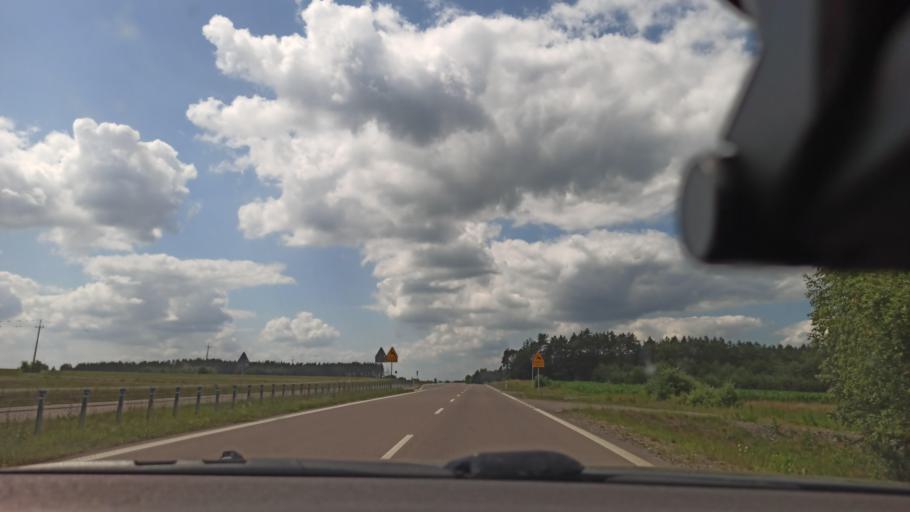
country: PL
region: Podlasie
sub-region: Powiat bialostocki
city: Turosn Koscielna
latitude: 53.0174
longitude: 22.9910
